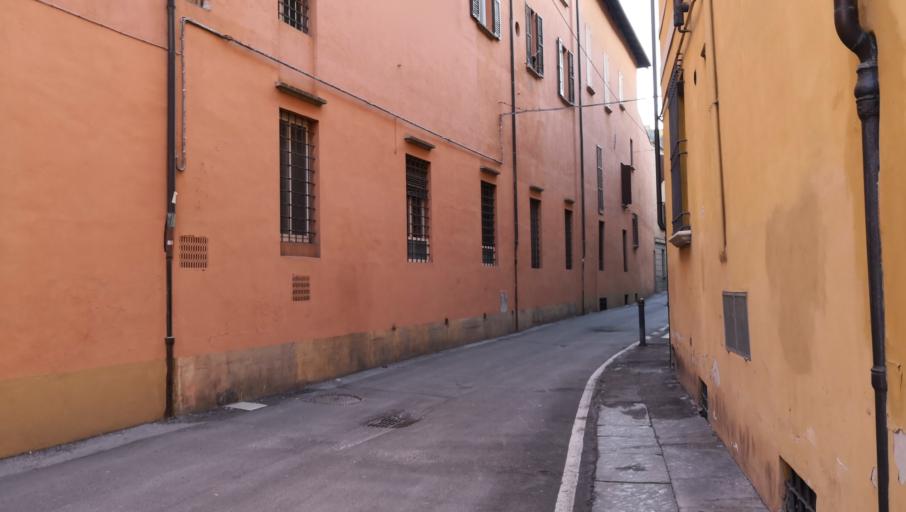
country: IT
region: Emilia-Romagna
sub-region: Provincia di Bologna
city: Bologna
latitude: 44.4904
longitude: 11.3370
